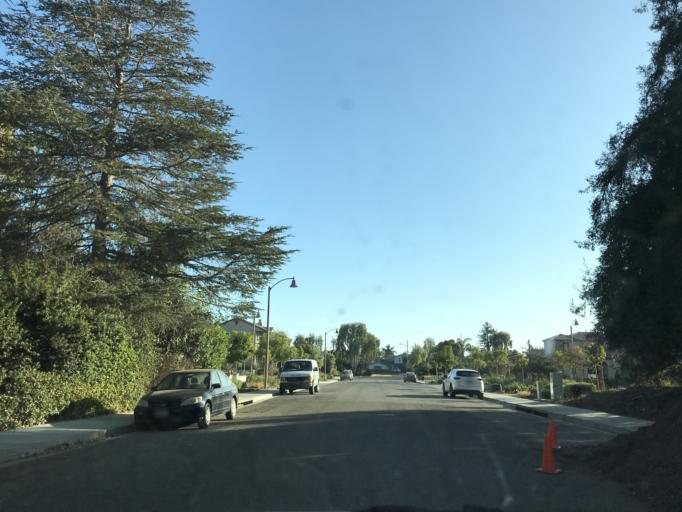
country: US
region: California
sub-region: Santa Barbara County
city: Goleta
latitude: 34.4496
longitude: -119.8109
